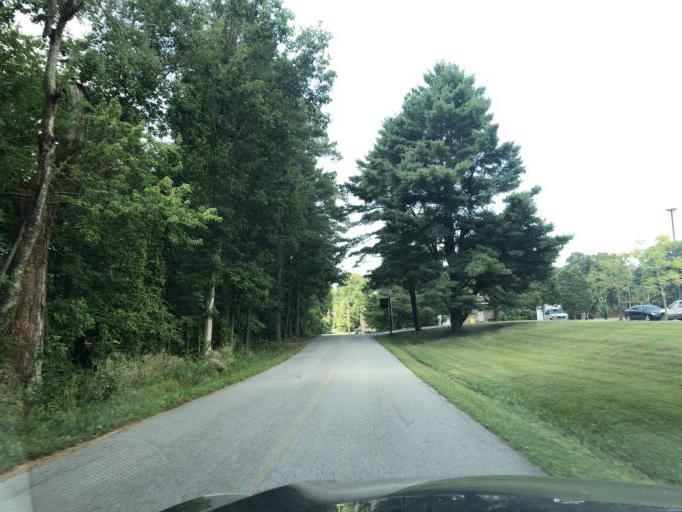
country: US
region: Tennessee
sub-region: Franklin County
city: Sewanee
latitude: 35.1953
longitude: -85.9252
